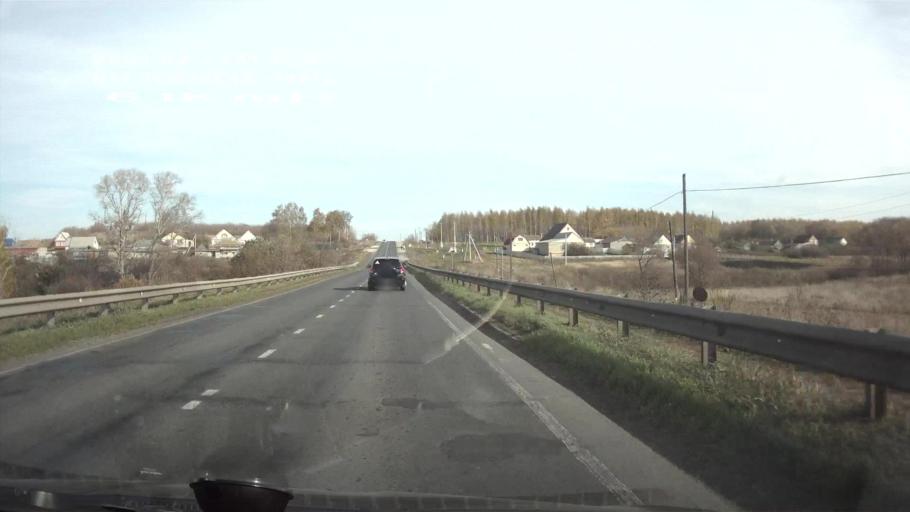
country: RU
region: Mordoviya
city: Atyashevo
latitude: 54.5616
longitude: 45.9789
